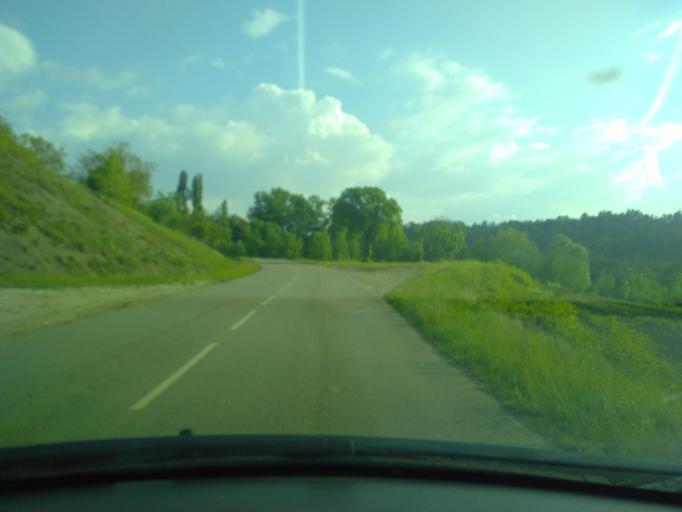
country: FR
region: Rhone-Alpes
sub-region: Departement de la Drome
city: Die
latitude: 44.6831
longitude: 5.4693
